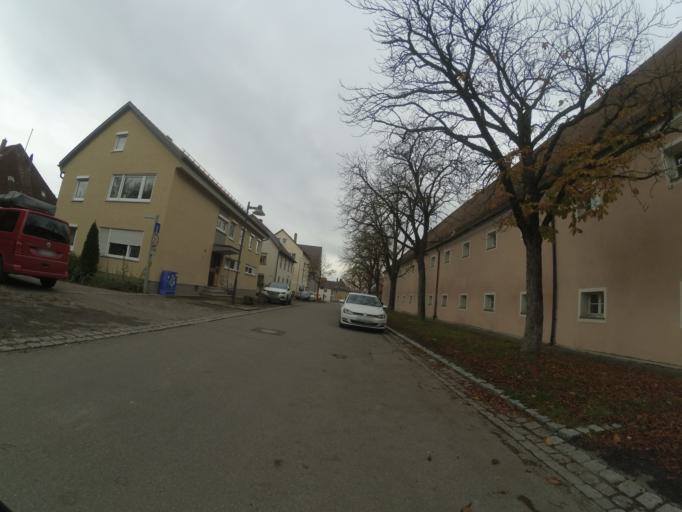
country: DE
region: Baden-Wuerttemberg
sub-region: Tuebingen Region
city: Ulm
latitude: 48.3615
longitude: 9.9900
